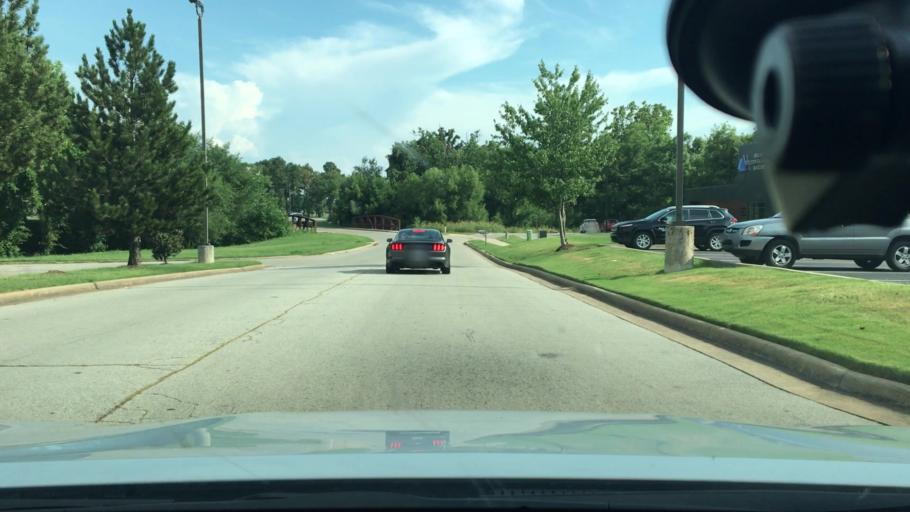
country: US
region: Arkansas
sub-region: Benton County
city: Bentonville
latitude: 36.3334
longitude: -94.1872
